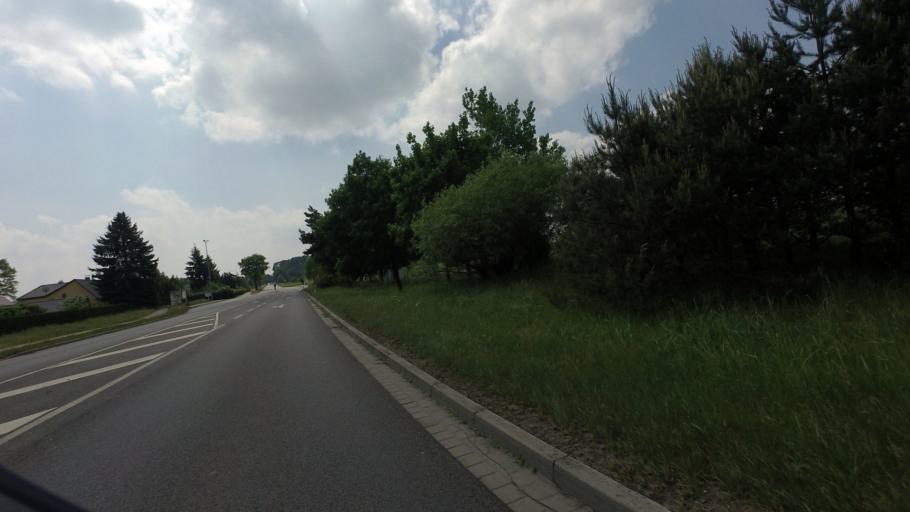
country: DE
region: Brandenburg
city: Cottbus
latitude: 51.6855
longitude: 14.3590
